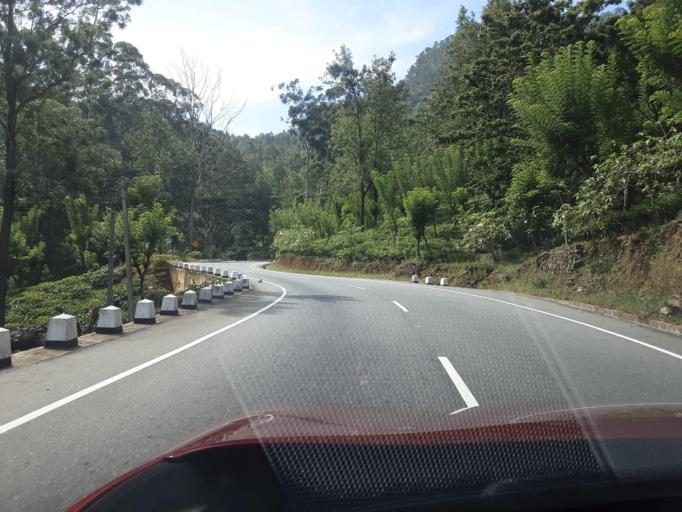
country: LK
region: Uva
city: Badulla
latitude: 6.9590
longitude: 81.1073
